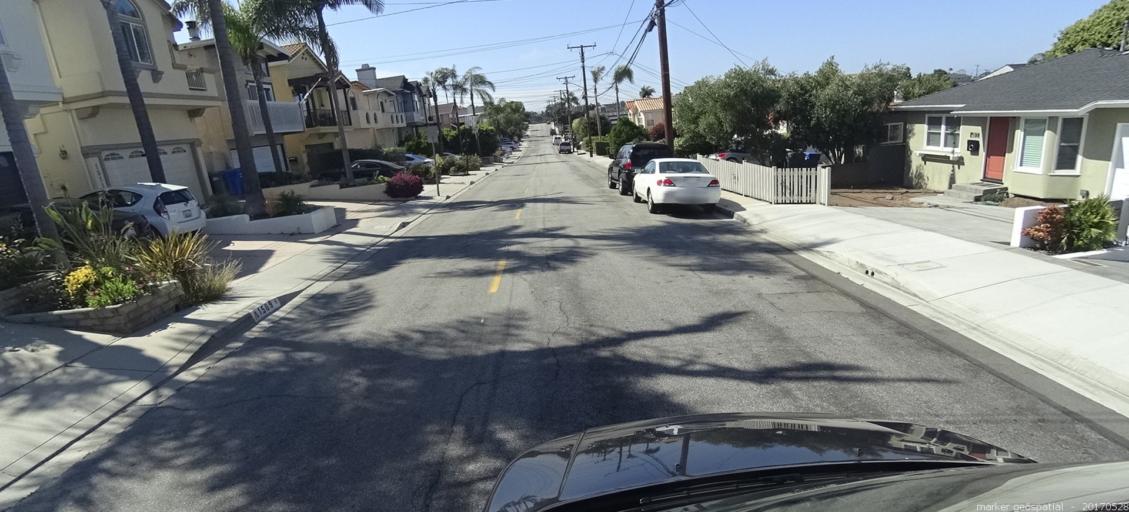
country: US
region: California
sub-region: Los Angeles County
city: Hermosa Beach
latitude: 33.8672
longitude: -118.3868
